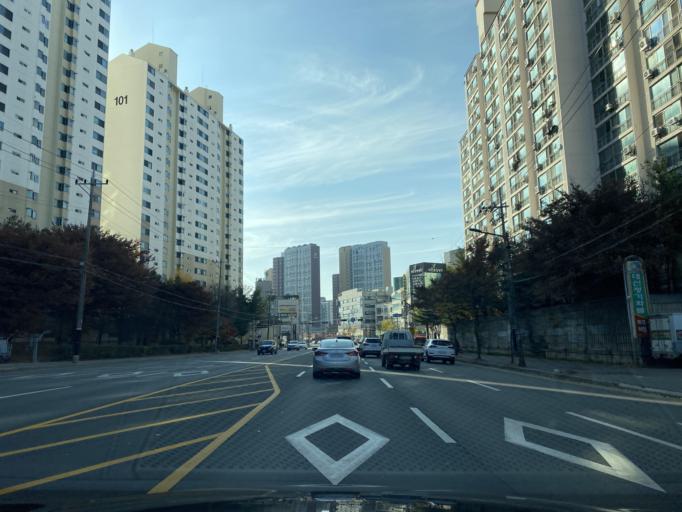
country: KR
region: Chungcheongnam-do
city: Cheonan
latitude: 36.7935
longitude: 127.1246
